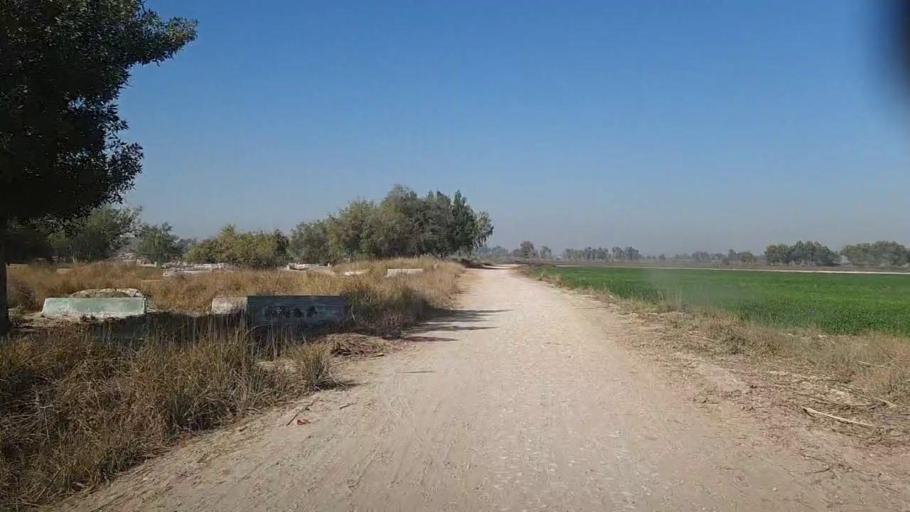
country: PK
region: Sindh
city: Khairpur
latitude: 28.0033
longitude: 69.6488
